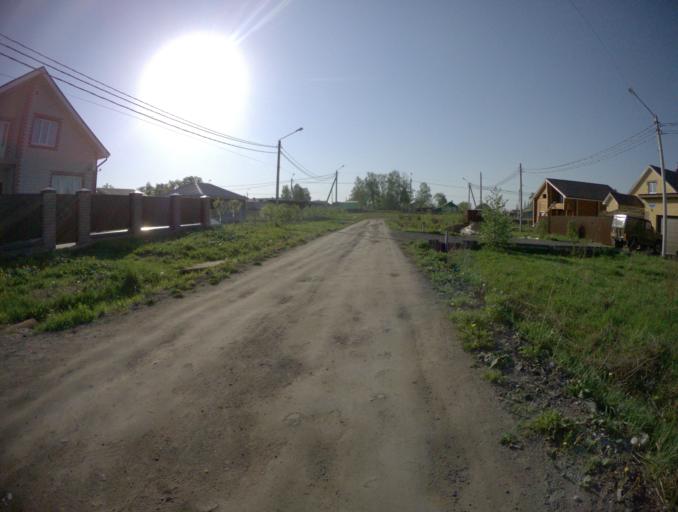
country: RU
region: Vladimir
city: Novovyazniki
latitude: 56.2250
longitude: 42.1865
